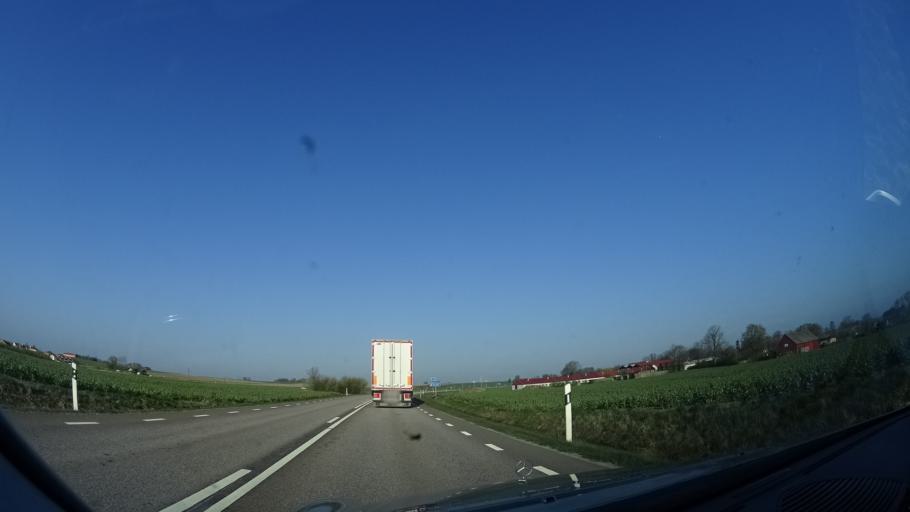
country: SE
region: Skane
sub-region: Eslovs Kommun
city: Eslov
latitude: 55.8537
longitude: 13.2819
